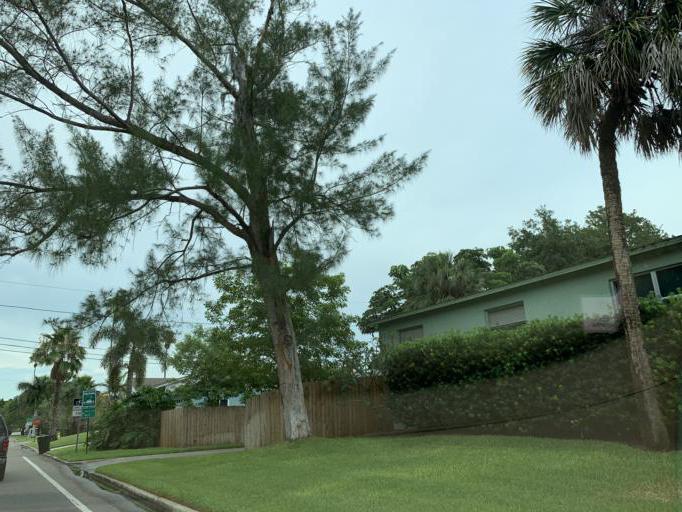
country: US
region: Florida
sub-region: Pinellas County
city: Gandy
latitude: 27.8205
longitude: -82.6045
